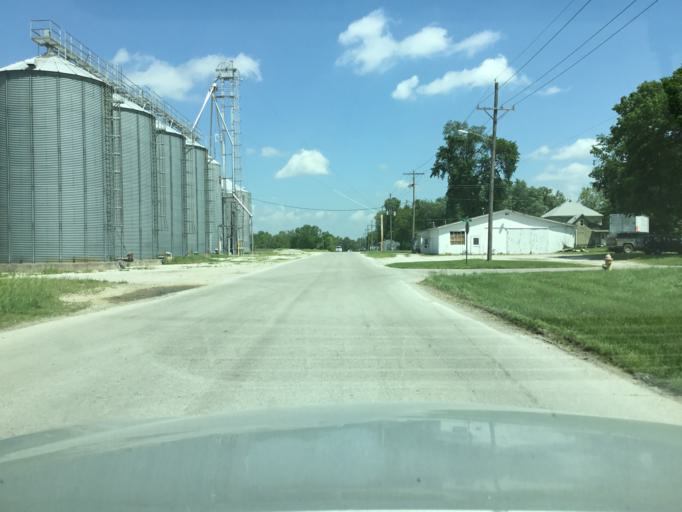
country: US
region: Kansas
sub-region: Labette County
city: Parsons
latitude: 37.3433
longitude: -95.2657
